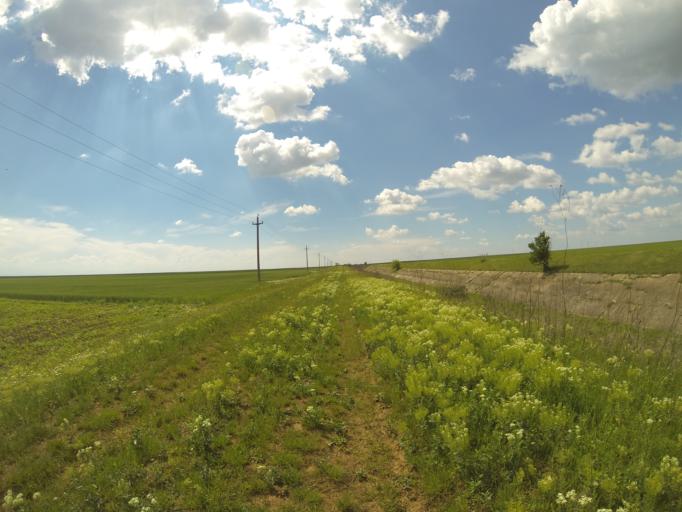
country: RO
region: Dolj
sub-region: Comuna Dranicu
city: Dranic
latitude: 44.0150
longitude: 23.8022
